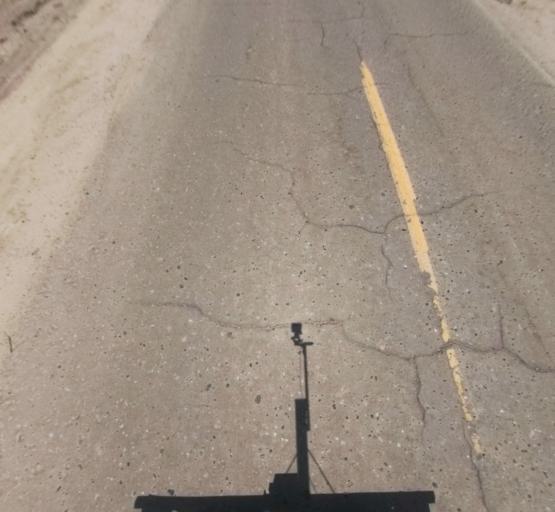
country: US
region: California
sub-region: Fresno County
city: Biola
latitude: 36.8314
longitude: -120.1150
